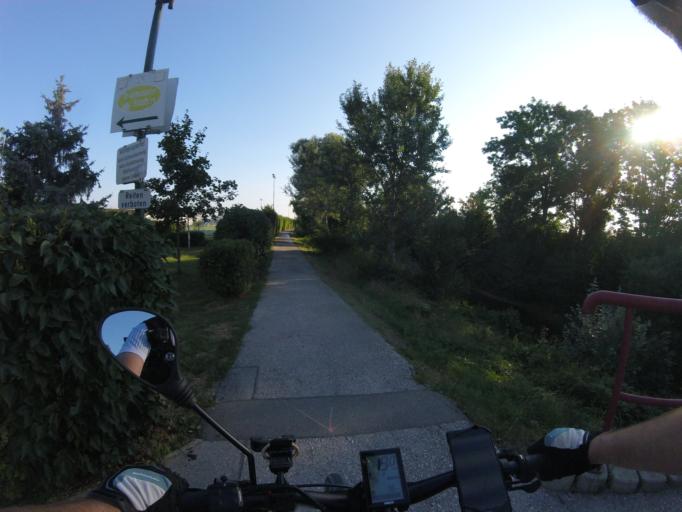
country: AT
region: Lower Austria
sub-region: Politischer Bezirk Baden
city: Trumau
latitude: 47.9979
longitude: 16.3496
